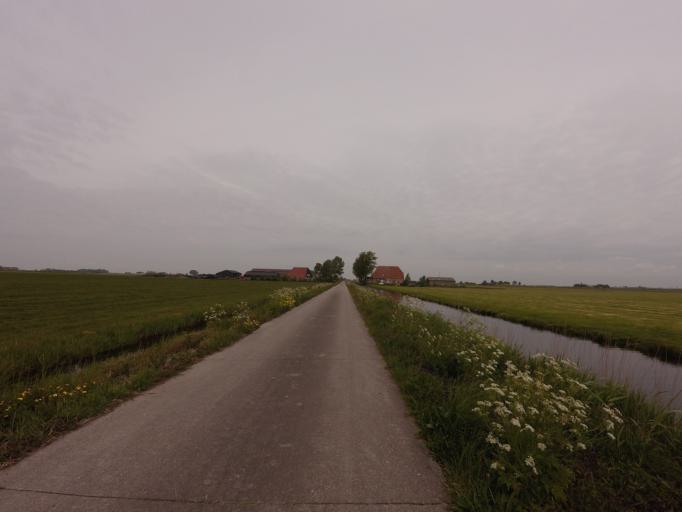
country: NL
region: Friesland
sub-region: Sudwest Fryslan
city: Workum
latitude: 53.0169
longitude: 5.4609
